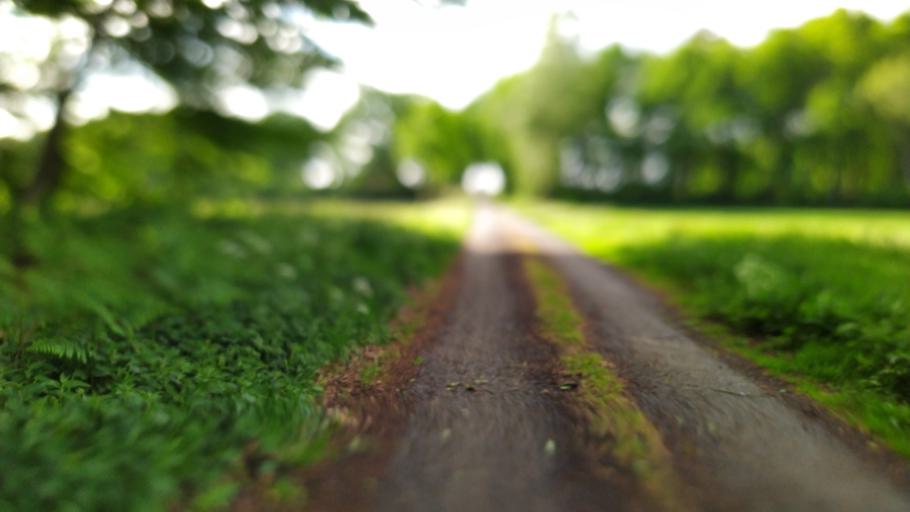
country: DE
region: Lower Saxony
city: Farven
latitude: 53.4448
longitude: 9.2824
